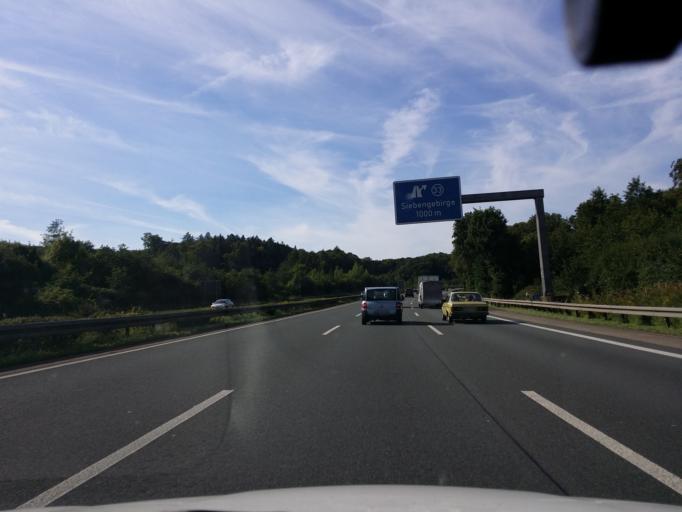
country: DE
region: North Rhine-Westphalia
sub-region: Regierungsbezirk Koln
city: Bad Honnef
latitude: 50.6788
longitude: 7.2841
